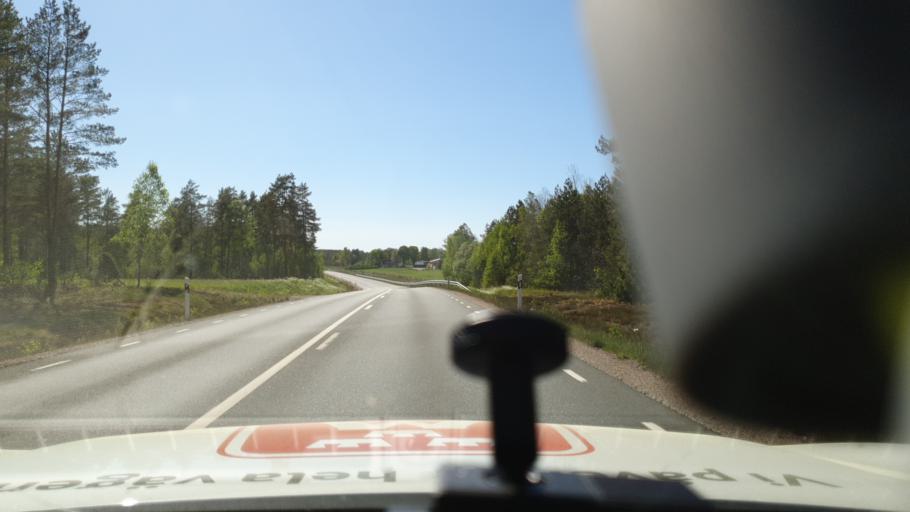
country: SE
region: Kalmar
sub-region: Hultsfreds Kommun
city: Virserum
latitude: 57.3994
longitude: 15.4154
